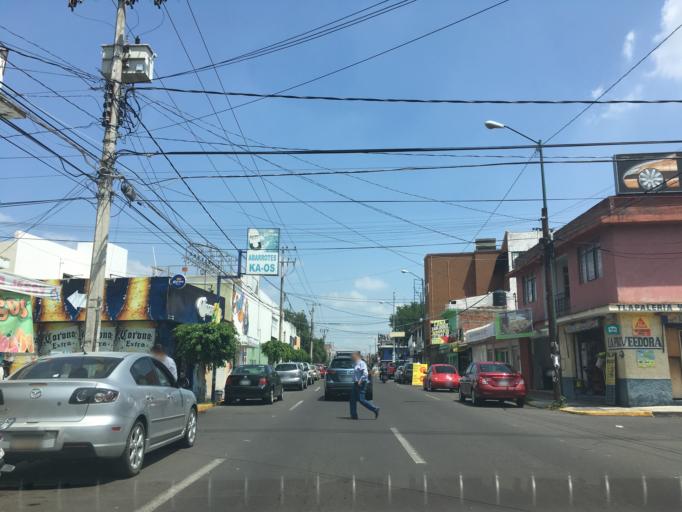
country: MX
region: Michoacan
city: Morelia
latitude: 19.6900
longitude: -101.1906
